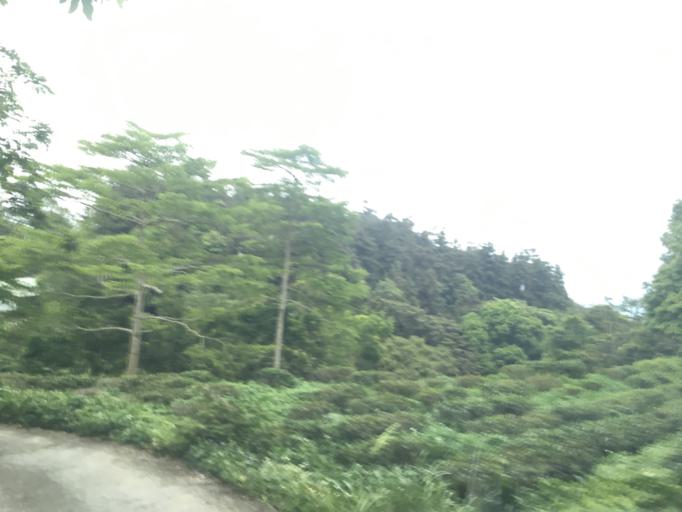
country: TW
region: Taiwan
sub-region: Nantou
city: Puli
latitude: 23.9651
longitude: 120.8378
